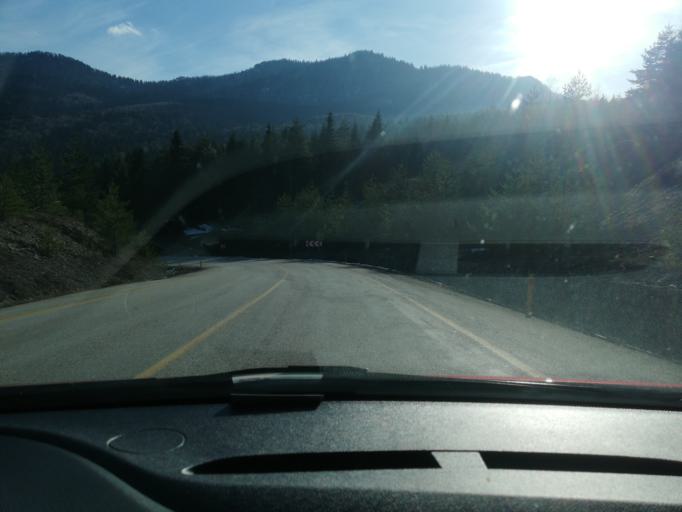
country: TR
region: Kastamonu
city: Senpazar
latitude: 41.7853
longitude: 33.1387
